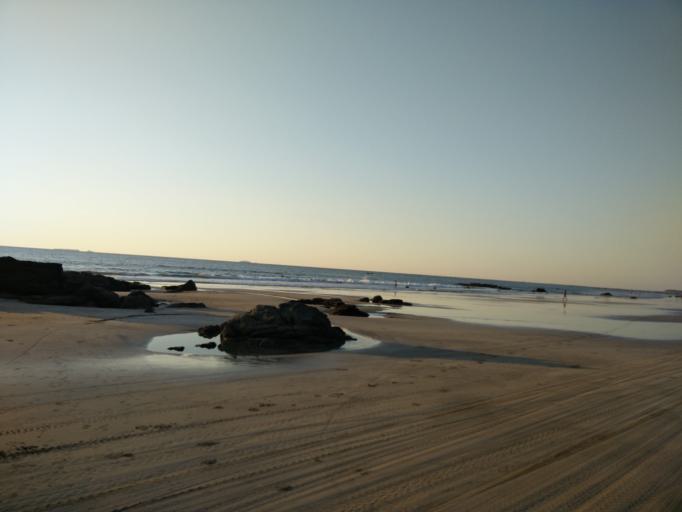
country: MM
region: Ayeyarwady
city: Pathein
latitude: 16.8236
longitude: 94.3968
